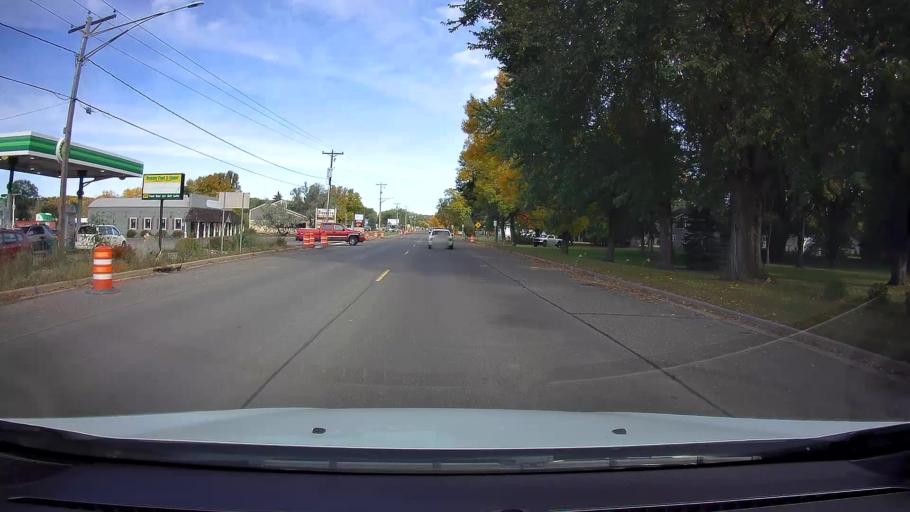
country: US
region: Wisconsin
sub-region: Polk County
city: Saint Croix Falls
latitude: 45.3547
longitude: -92.6373
